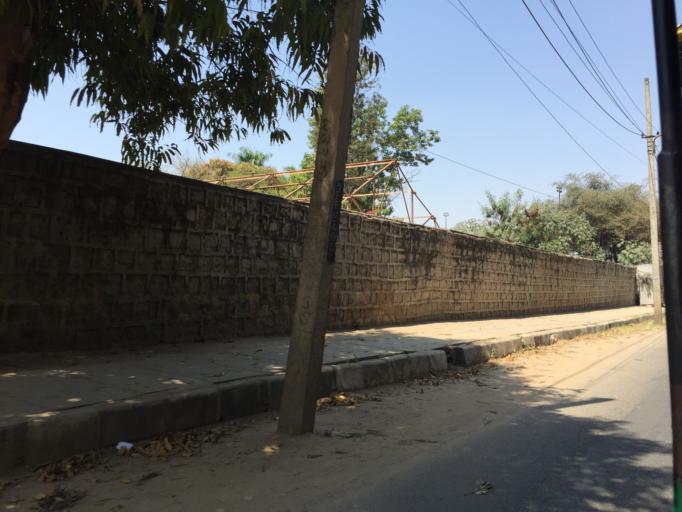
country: IN
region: Karnataka
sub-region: Bangalore Urban
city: Bangalore
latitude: 12.9833
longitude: 77.6226
